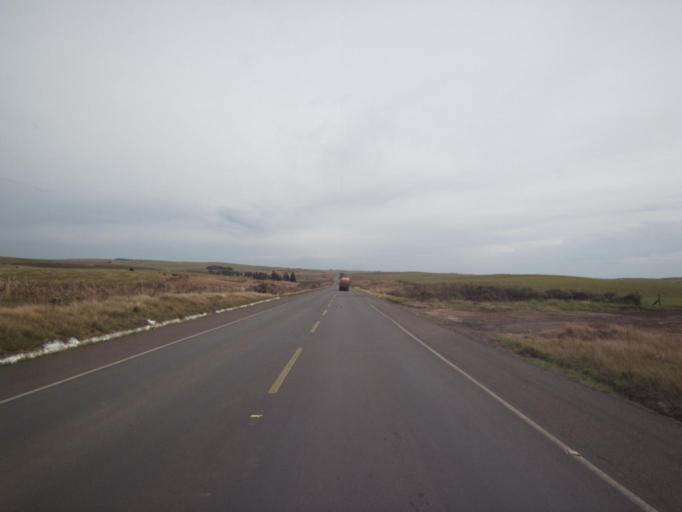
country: BR
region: Parana
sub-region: Palmas
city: Palmas
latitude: -26.7214
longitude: -51.6248
